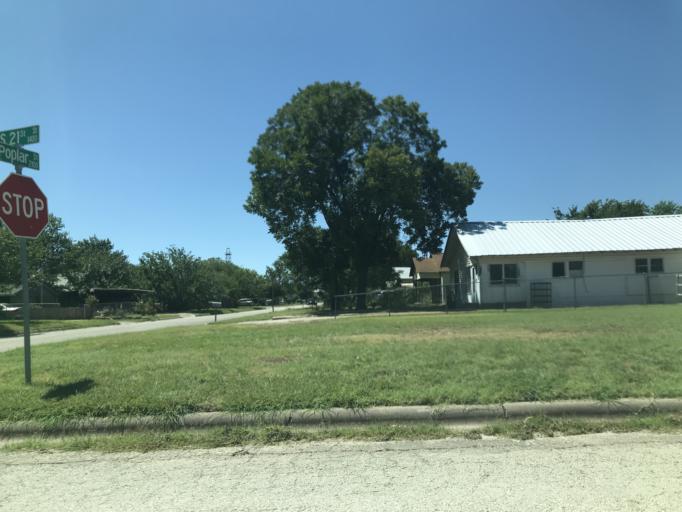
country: US
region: Texas
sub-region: Taylor County
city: Abilene
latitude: 32.4231
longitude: -99.7398
